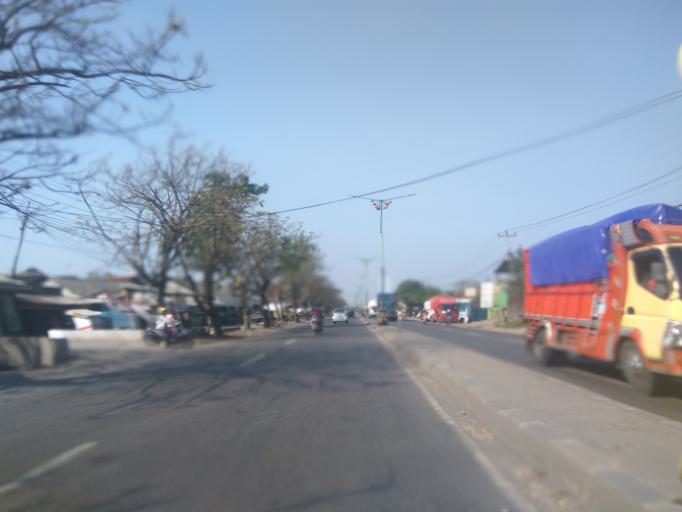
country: ID
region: Central Java
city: Mranggen
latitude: -6.9470
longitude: 110.4927
